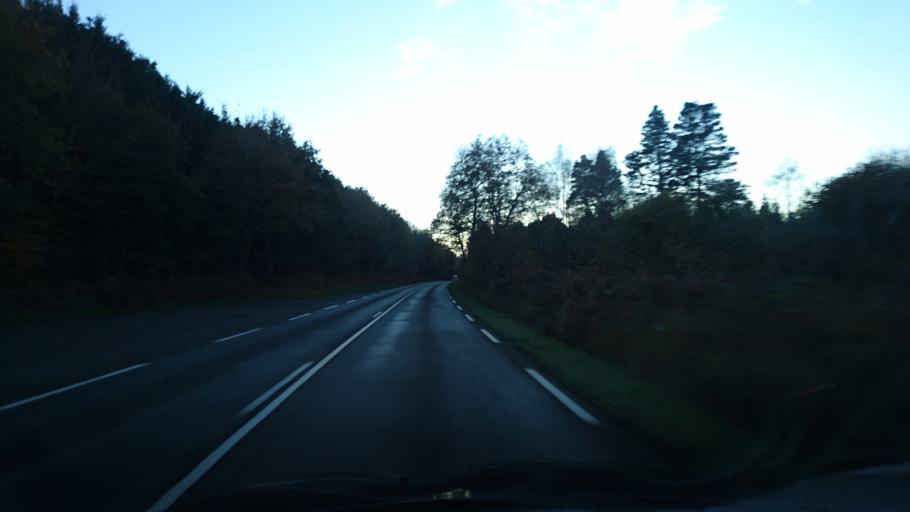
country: FR
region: Brittany
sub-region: Departement du Finistere
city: Moelan-sur-Mer
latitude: 47.8311
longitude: -3.5976
